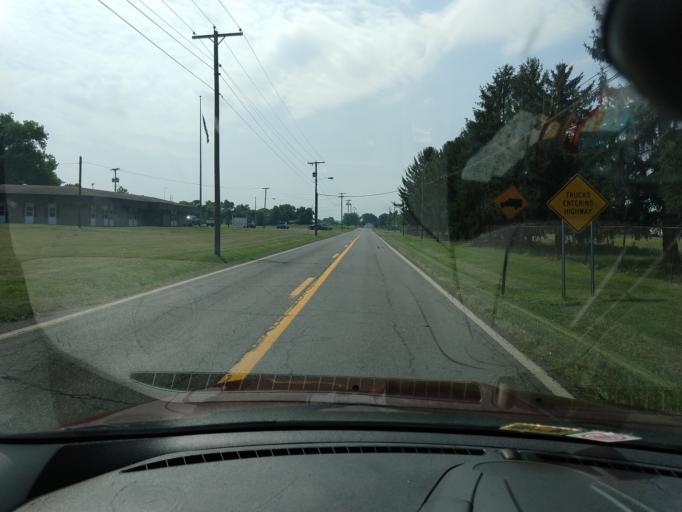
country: US
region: West Virginia
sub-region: Mason County
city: New Haven
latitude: 38.9592
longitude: -81.9247
